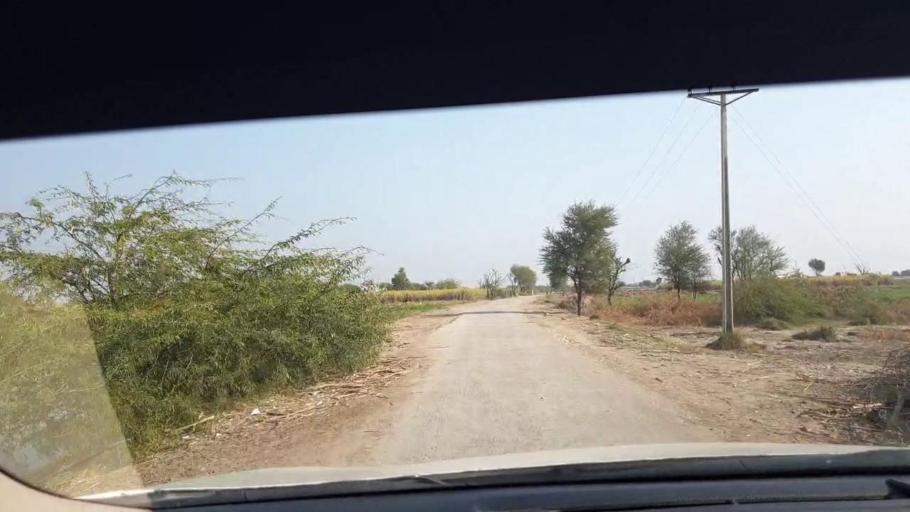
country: PK
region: Sindh
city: Berani
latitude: 25.8209
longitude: 68.7707
